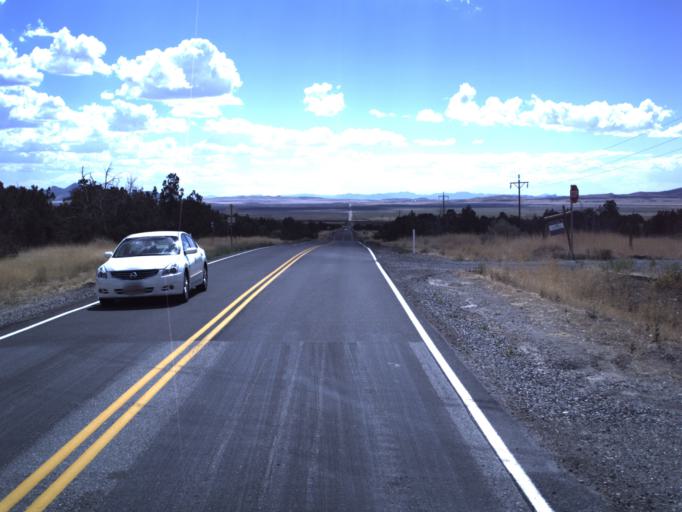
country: US
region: Utah
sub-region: Tooele County
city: Grantsville
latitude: 40.3199
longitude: -112.6278
